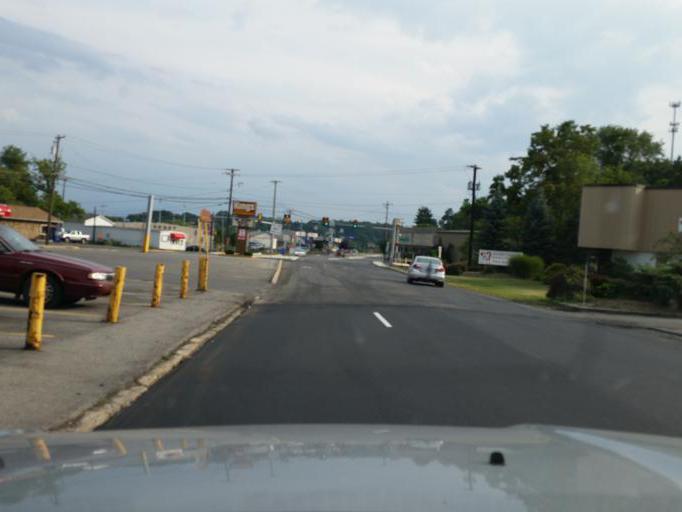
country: US
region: Pennsylvania
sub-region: Blair County
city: Altoona
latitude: 40.4963
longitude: -78.4115
